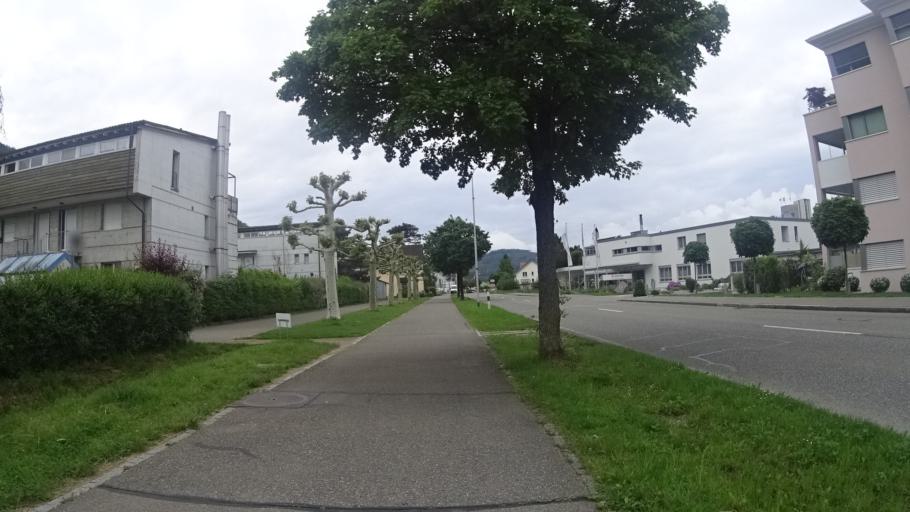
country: CH
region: Aargau
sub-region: Bezirk Baden
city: Wurenlingen
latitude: 47.5236
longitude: 8.2461
